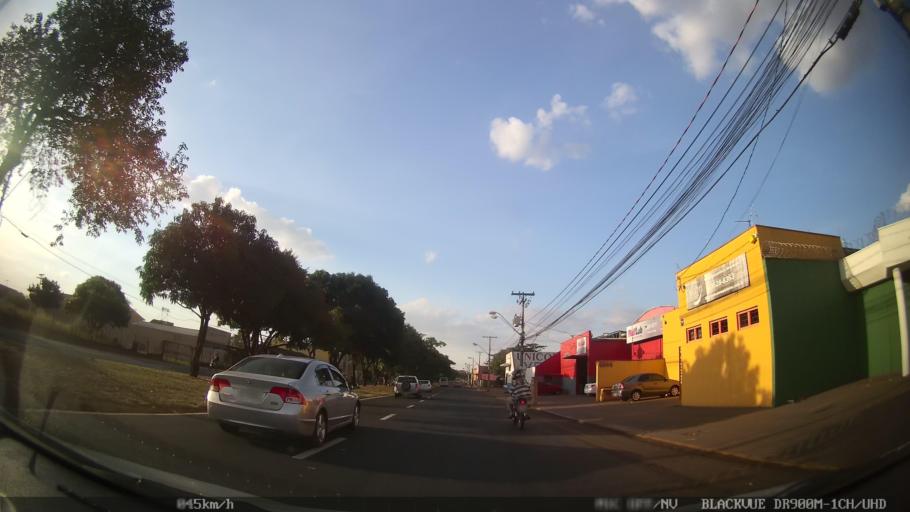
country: BR
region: Sao Paulo
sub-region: Ribeirao Preto
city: Ribeirao Preto
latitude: -21.1341
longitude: -47.7956
